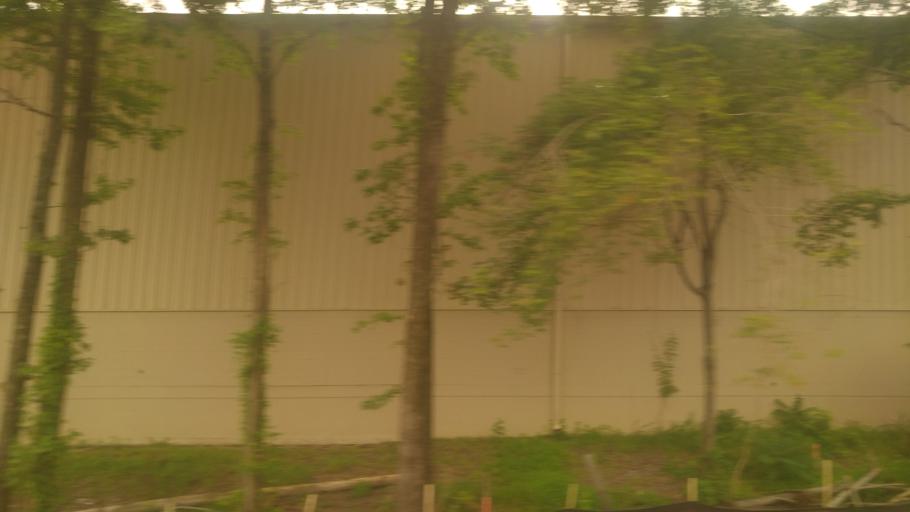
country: US
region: Virginia
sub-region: Henrico County
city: Laurel
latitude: 37.6260
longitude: -77.5000
